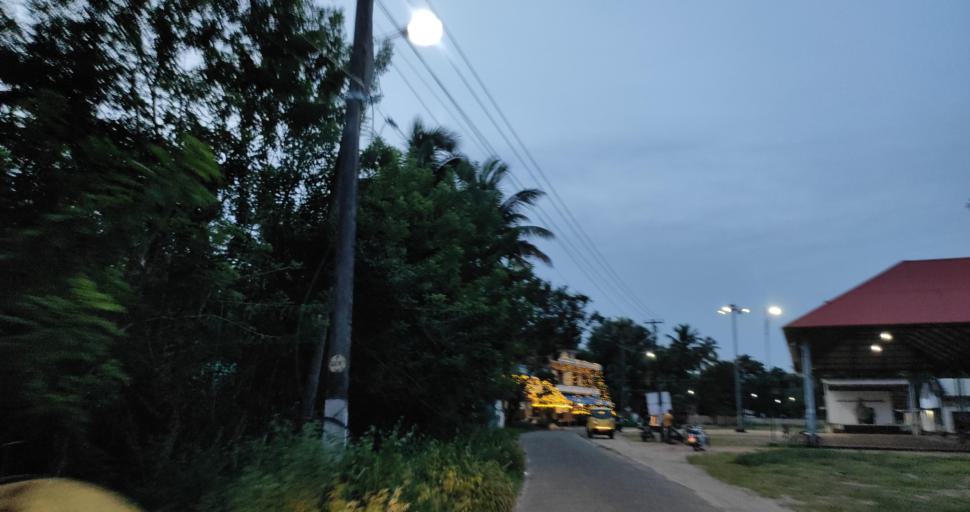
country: IN
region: Kerala
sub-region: Alappuzha
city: Vayalar
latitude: 9.7002
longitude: 76.3133
